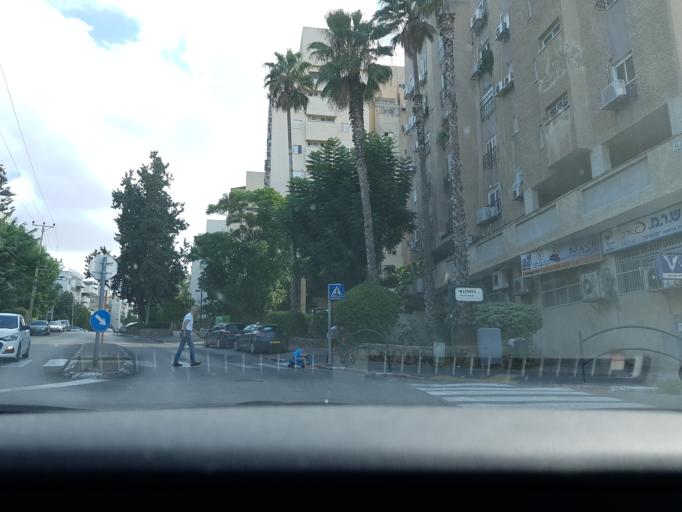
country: IL
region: Central District
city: Ness Ziona
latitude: 31.9036
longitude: 34.8119
